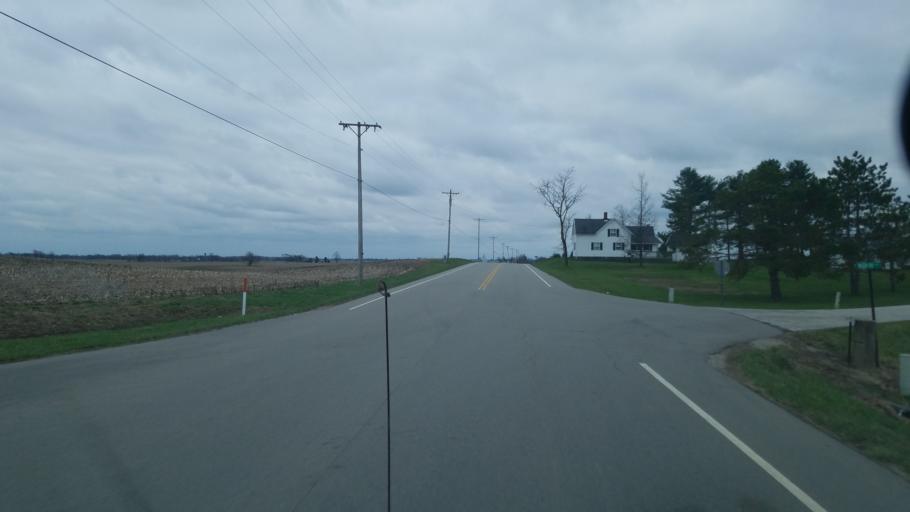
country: US
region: Ohio
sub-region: Fayette County
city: Washington Court House
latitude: 39.5675
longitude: -83.5056
